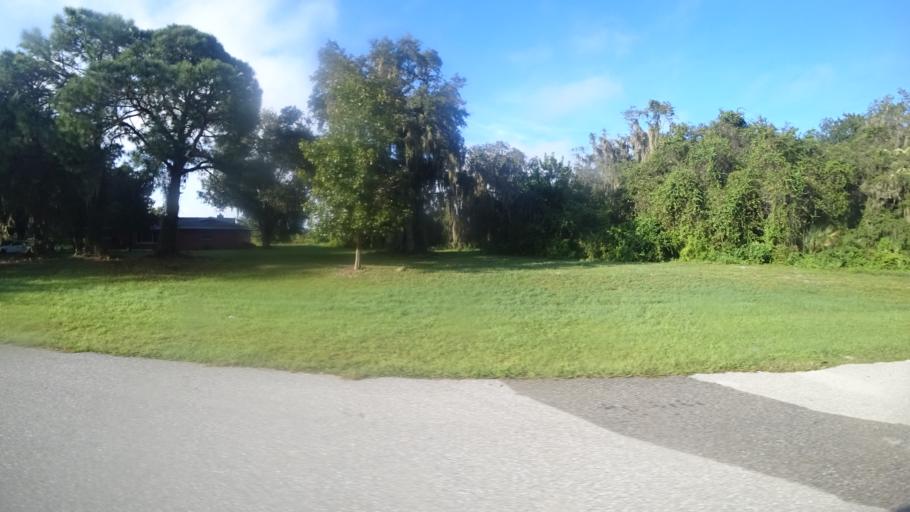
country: US
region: Florida
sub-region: Manatee County
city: Ellenton
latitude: 27.5387
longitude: -82.4552
